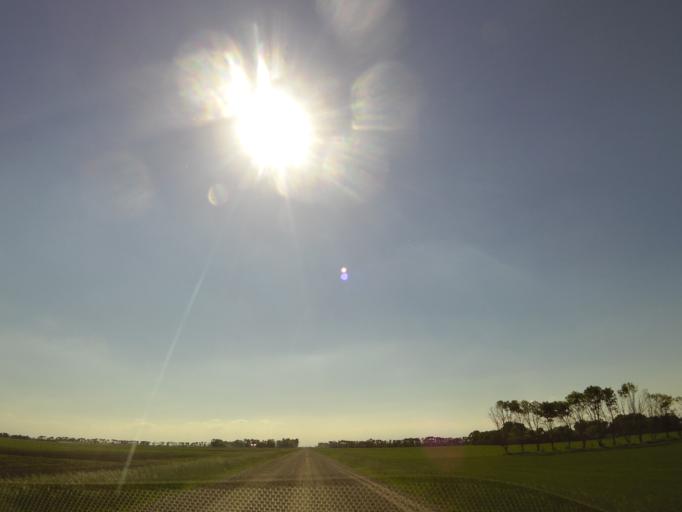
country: US
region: North Dakota
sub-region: Walsh County
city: Grafton
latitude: 48.3534
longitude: -97.2424
